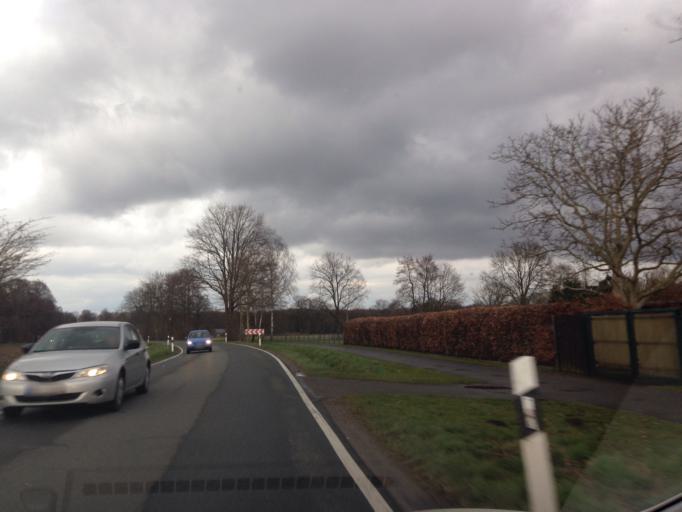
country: DE
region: North Rhine-Westphalia
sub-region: Regierungsbezirk Munster
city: Senden
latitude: 51.8319
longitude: 7.5411
